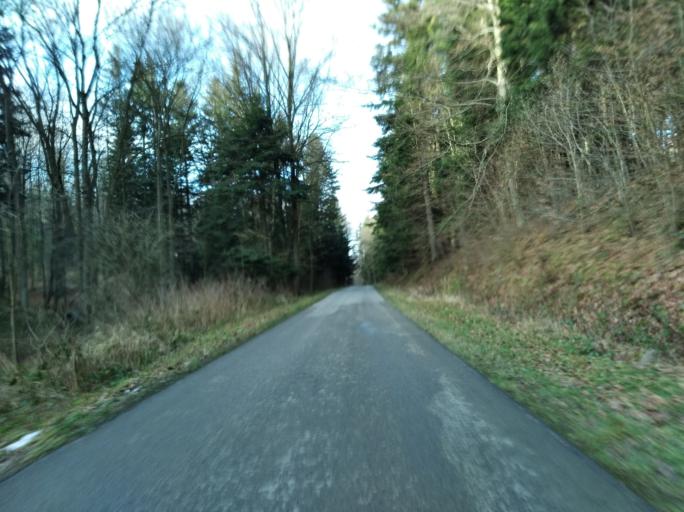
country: PL
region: Subcarpathian Voivodeship
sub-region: Powiat strzyzowski
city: Konieczkowa
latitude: 49.8265
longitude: 21.9422
